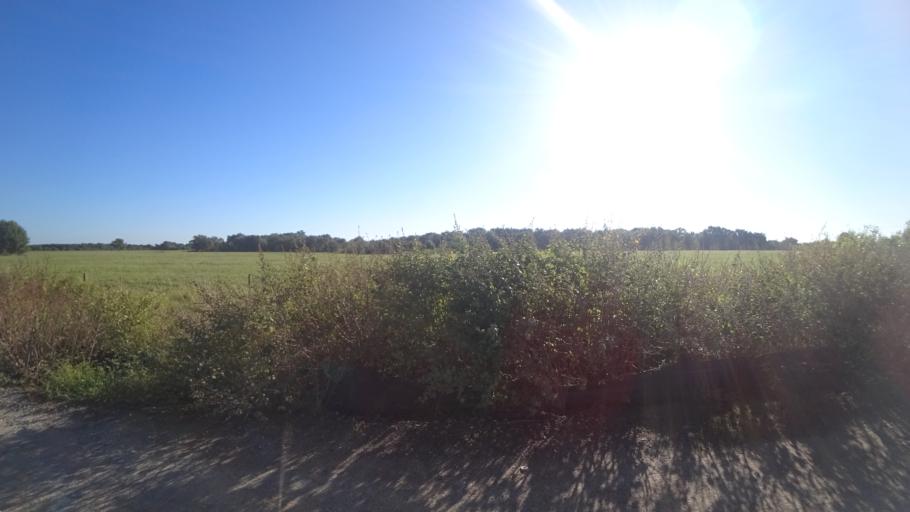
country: US
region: Florida
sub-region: Hillsborough County
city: Ruskin
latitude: 27.6254
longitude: -82.4880
